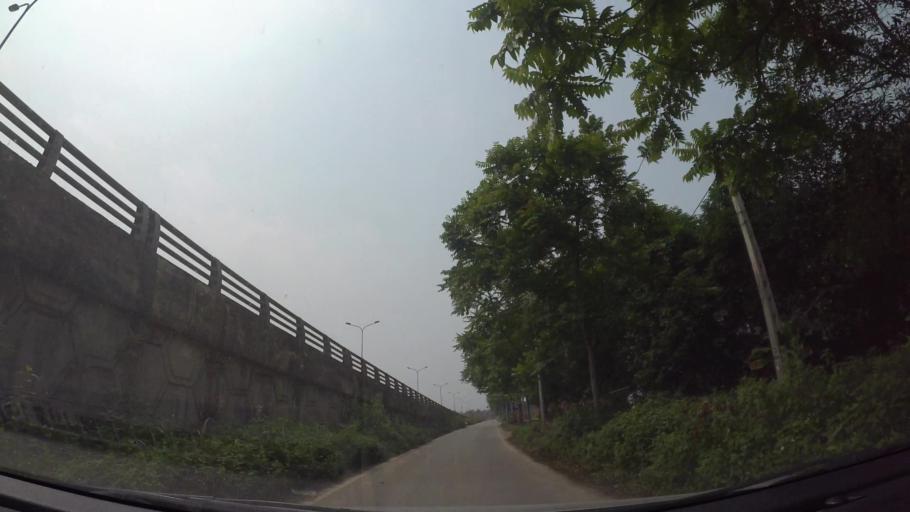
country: VN
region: Ha Noi
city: Lien Quan
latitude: 20.9890
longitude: 105.5363
